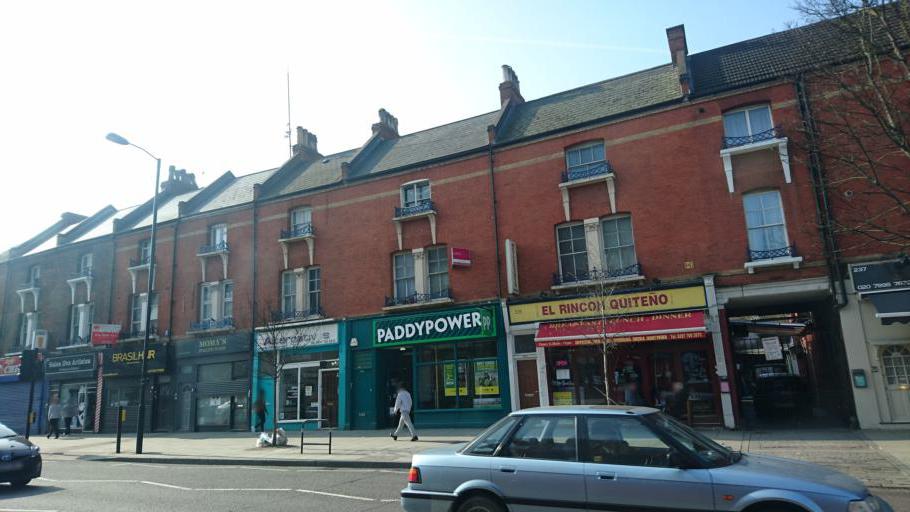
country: GB
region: England
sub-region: Greater London
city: Barnsbury
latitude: 51.5517
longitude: -0.1108
